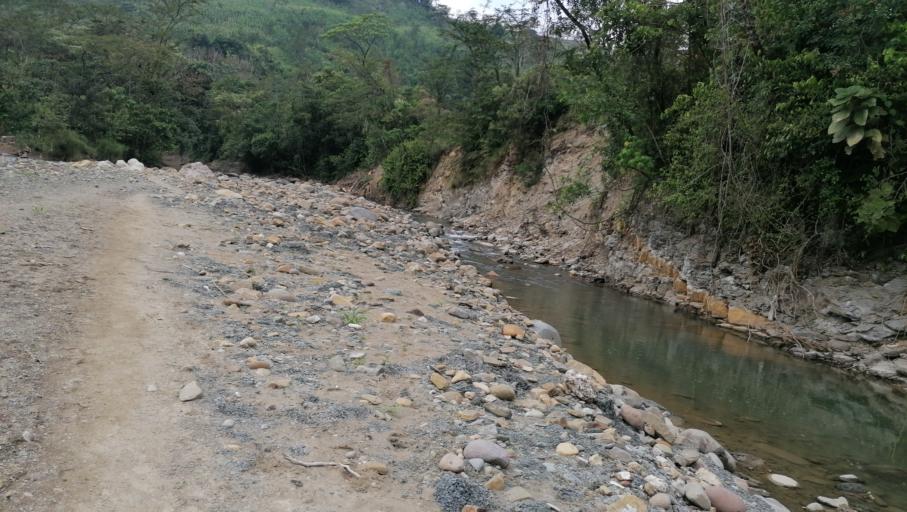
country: MX
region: Chiapas
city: Ocotepec
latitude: 17.2979
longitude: -93.2276
